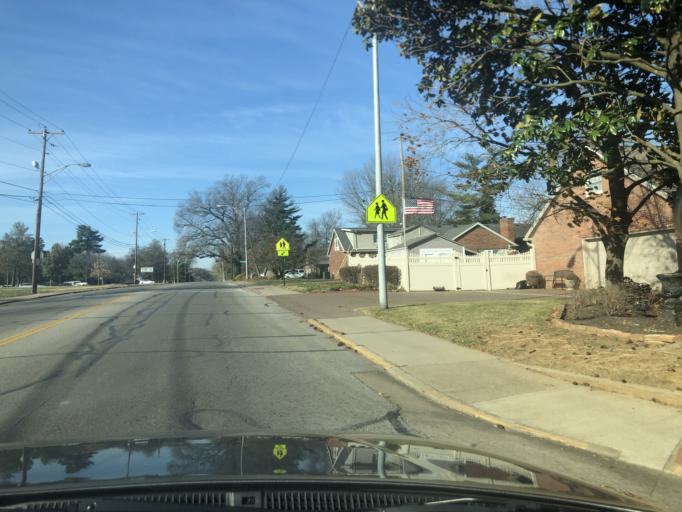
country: US
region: Indiana
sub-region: Warrick County
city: Newburgh
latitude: 37.9695
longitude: -87.4636
